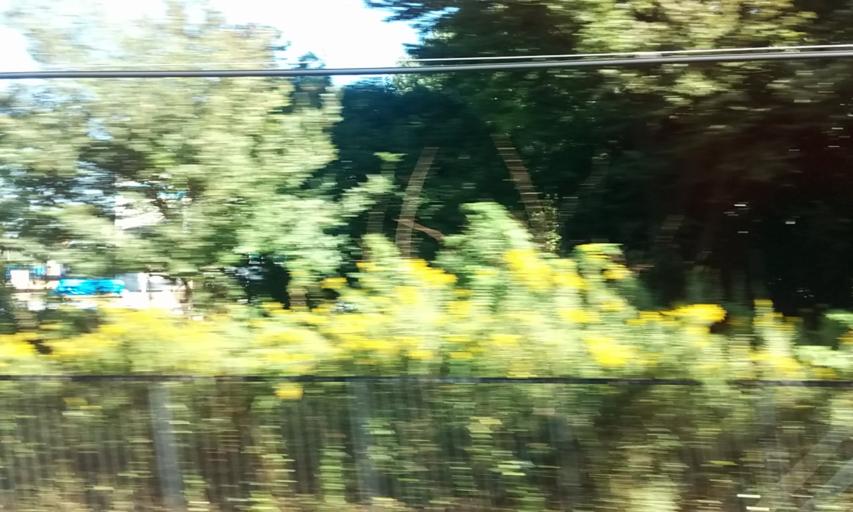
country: JP
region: Tokyo
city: Tanashicho
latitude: 35.7282
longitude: 139.5086
